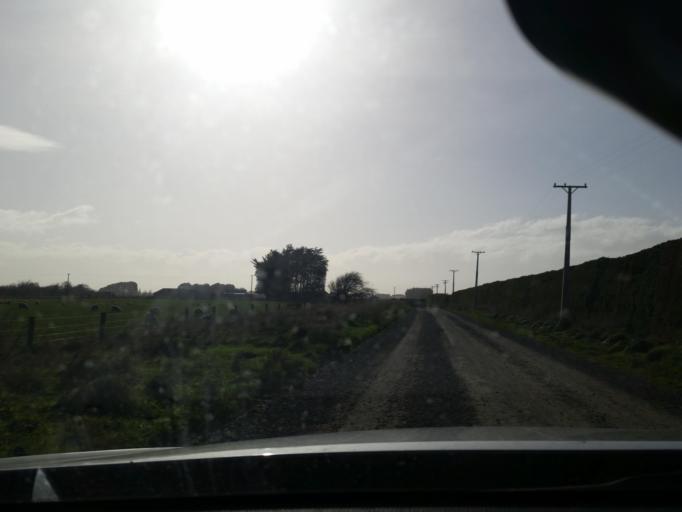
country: NZ
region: Southland
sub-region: Invercargill City
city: Invercargill
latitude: -46.2935
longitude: 168.2947
